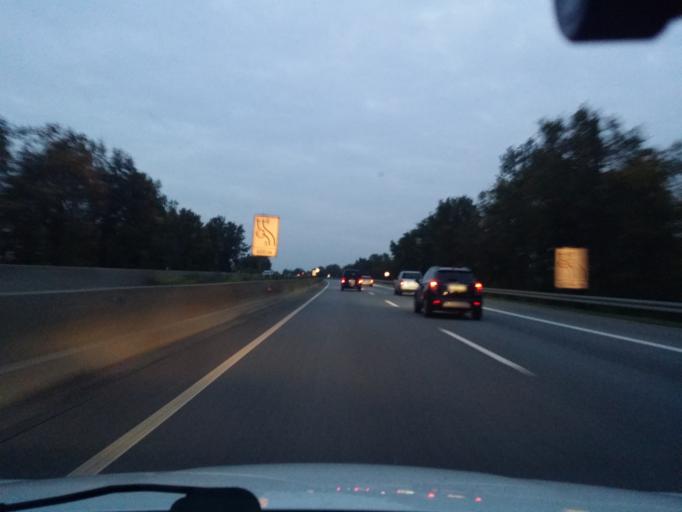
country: DE
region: Hesse
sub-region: Regierungsbezirk Darmstadt
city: Buttelborn
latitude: 49.9158
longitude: 8.5098
